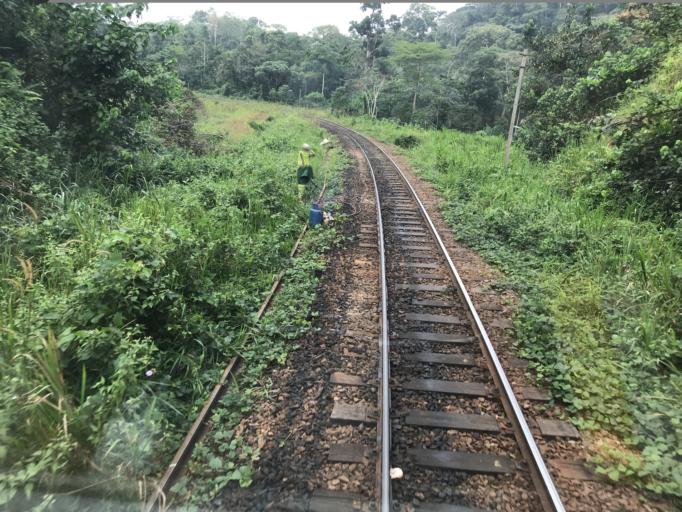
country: CM
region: Centre
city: Eseka
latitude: 3.5808
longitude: 10.8991
